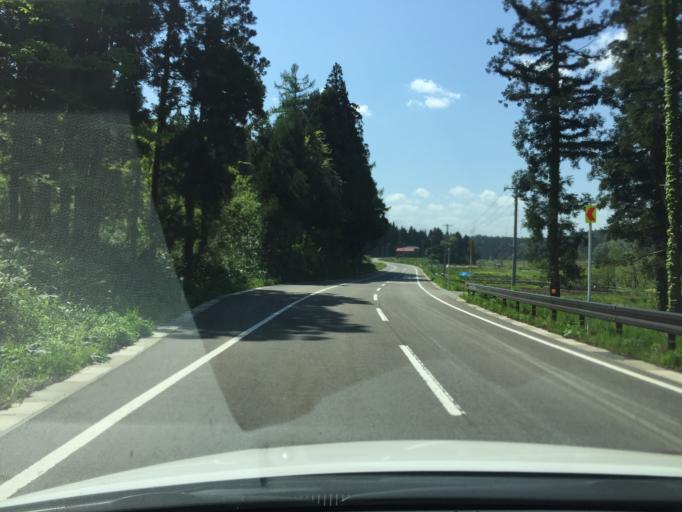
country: JP
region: Niigata
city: Kamo
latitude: 37.5711
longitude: 139.0836
